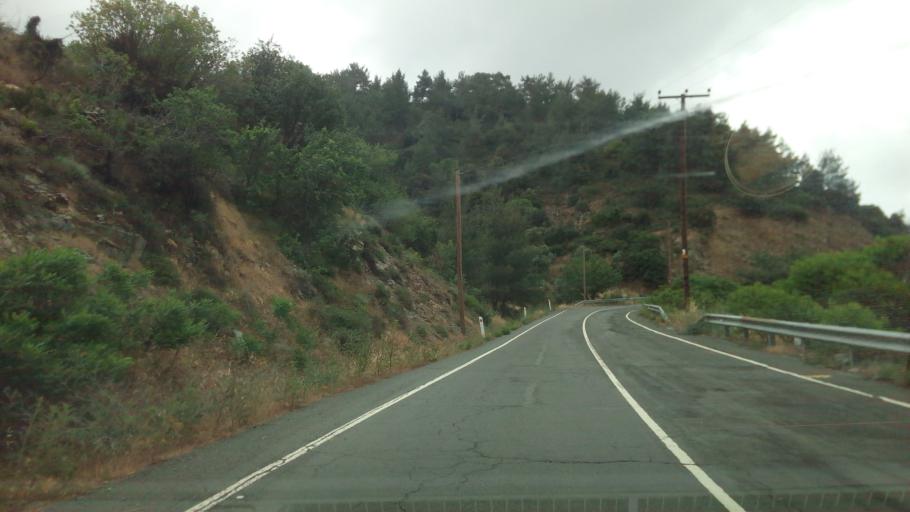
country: CY
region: Limassol
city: Pelendri
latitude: 34.8811
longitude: 32.9971
